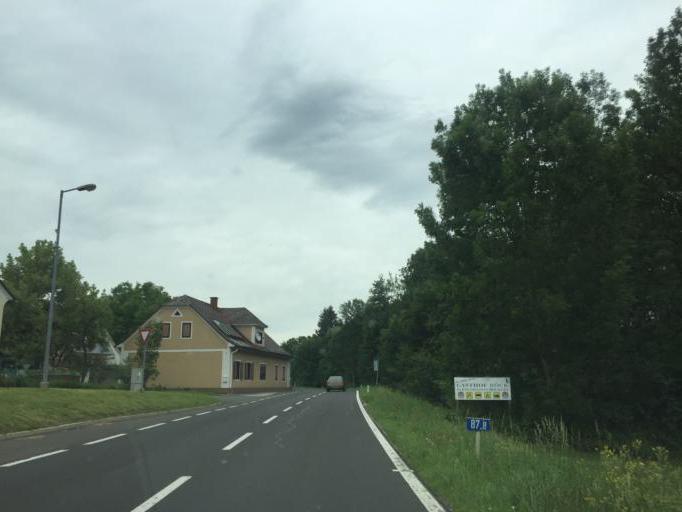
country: AT
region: Styria
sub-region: Politischer Bezirk Suedoststeiermark
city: Gosdorf
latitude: 46.7144
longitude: 15.7918
